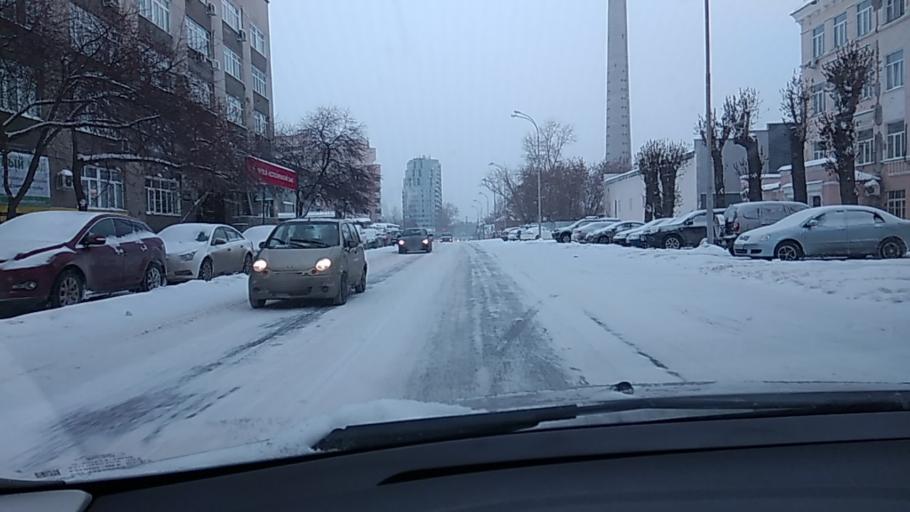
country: RU
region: Sverdlovsk
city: Yekaterinburg
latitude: 56.8207
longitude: 60.6087
